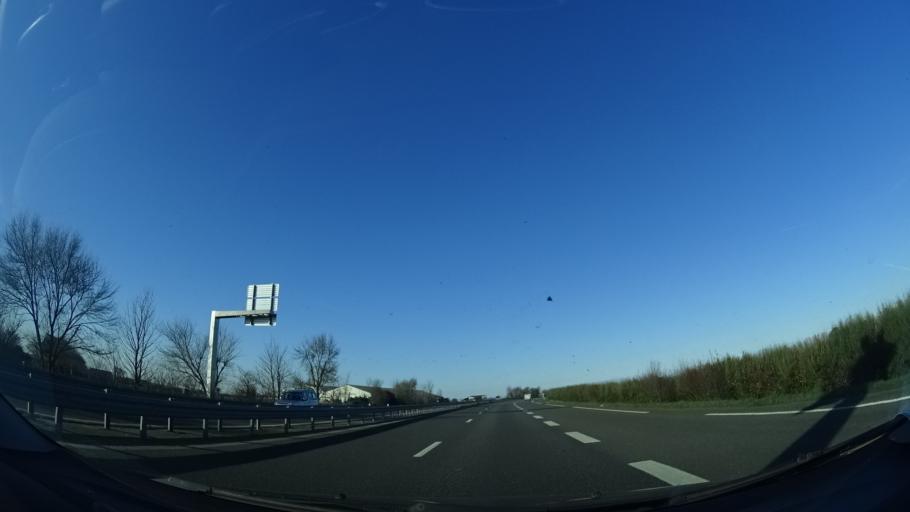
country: FR
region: Brittany
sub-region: Departement du Finistere
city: Taule
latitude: 48.6213
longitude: -3.9016
